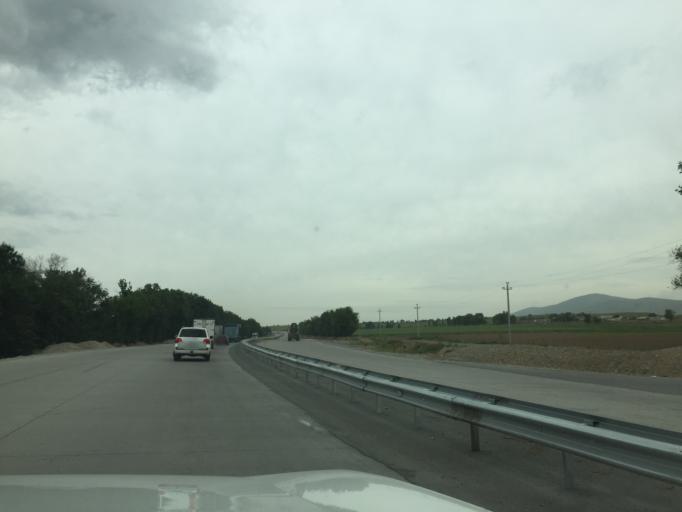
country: KZ
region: Ongtustik Qazaqstan
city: Sastobe
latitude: 42.5026
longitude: 69.9620
